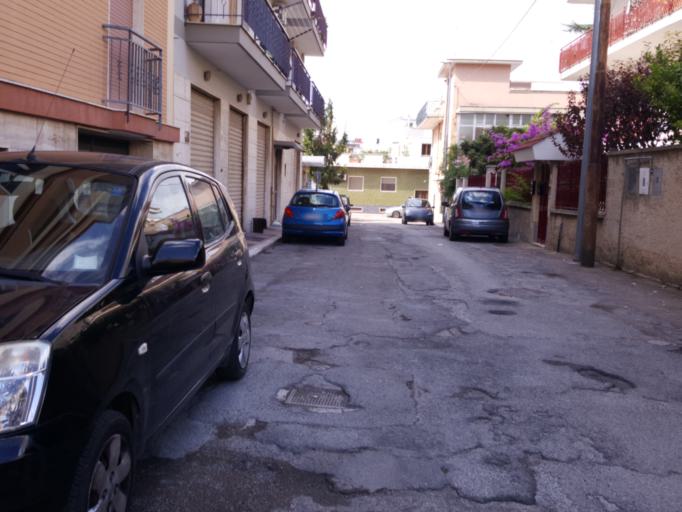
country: IT
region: Apulia
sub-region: Provincia di Bari
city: Triggiano
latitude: 41.0604
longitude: 16.9205
